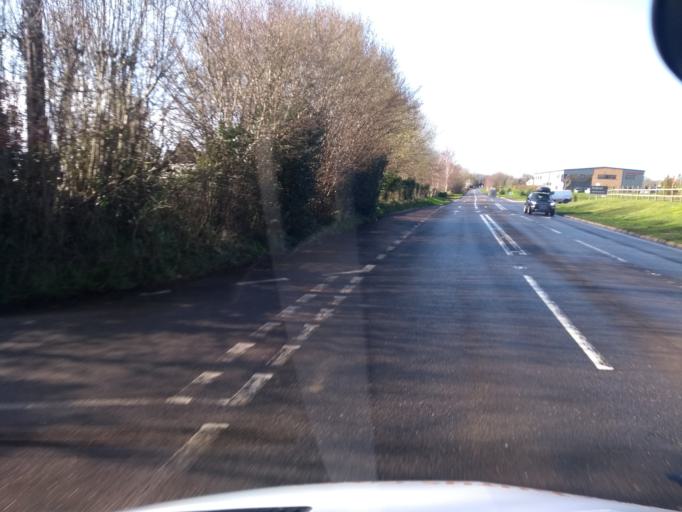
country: GB
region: England
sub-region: Somerset
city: South Petherton
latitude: 50.9339
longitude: -2.8179
